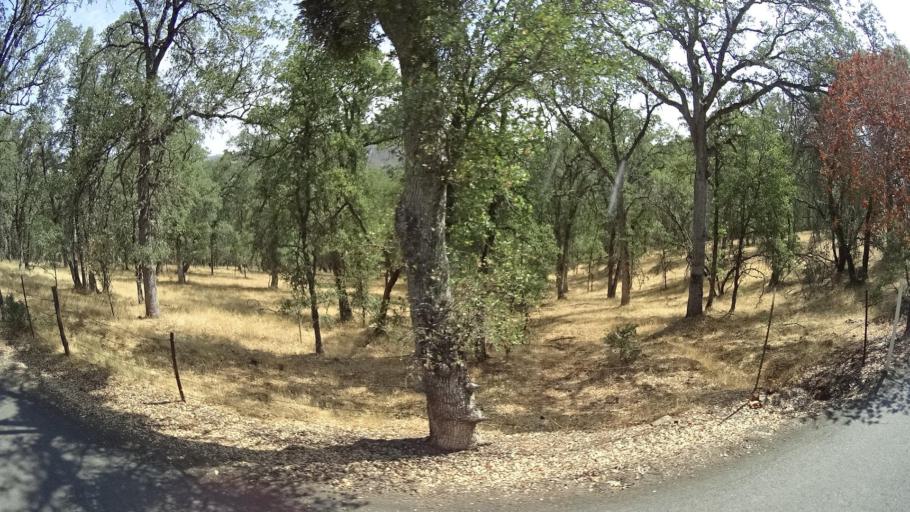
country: US
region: California
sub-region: Tuolumne County
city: Tuolumne City
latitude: 37.7123
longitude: -120.1801
